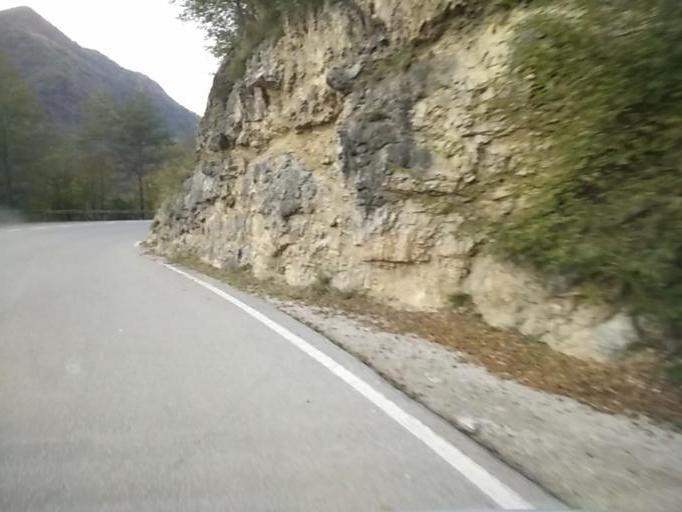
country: IT
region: Lombardy
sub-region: Provincia di Brescia
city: Valvestino
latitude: 45.7227
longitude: 10.6128
